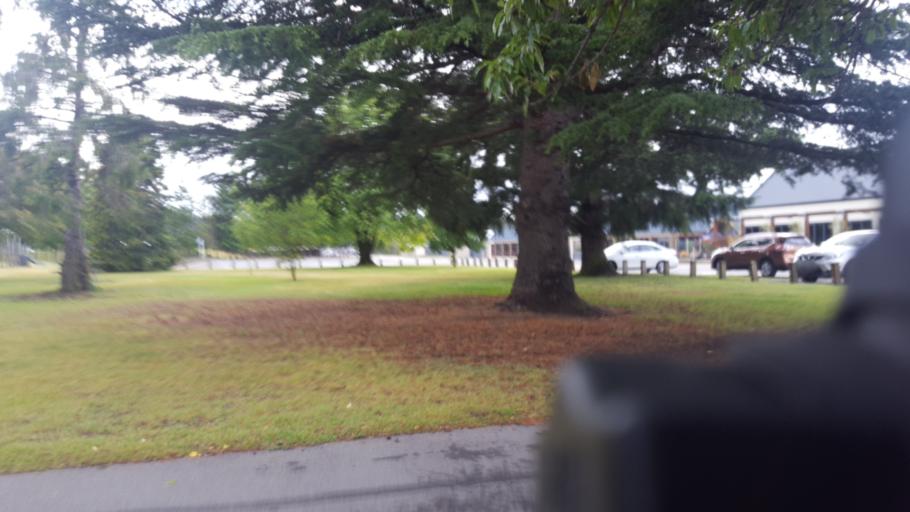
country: NZ
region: Otago
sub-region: Queenstown-Lakes District
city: Wanaka
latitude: -45.2452
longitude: 169.3817
